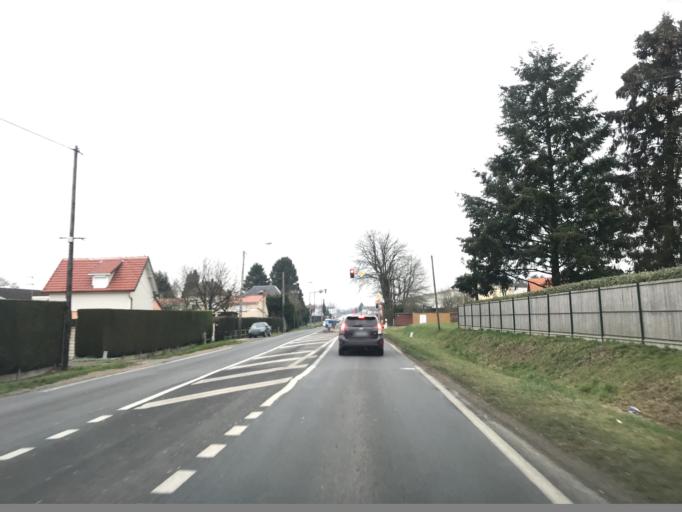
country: FR
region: Haute-Normandie
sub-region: Departement de la Seine-Maritime
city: Boos
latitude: 49.3952
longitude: 1.1849
